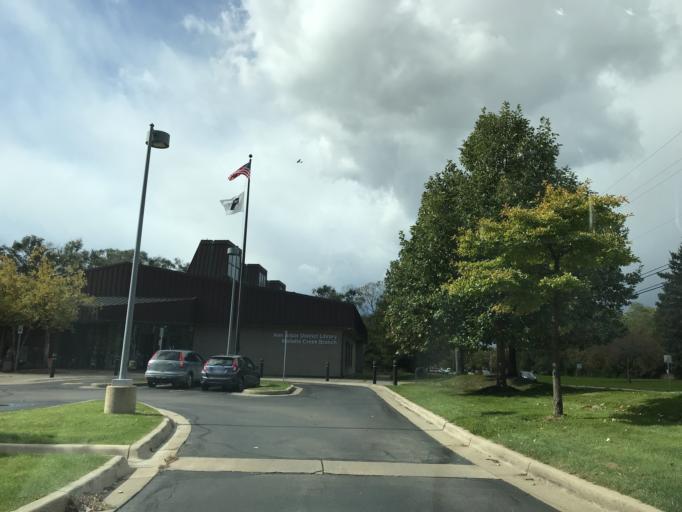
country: US
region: Michigan
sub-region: Washtenaw County
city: Ann Arbor
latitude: 42.2439
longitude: -83.7172
